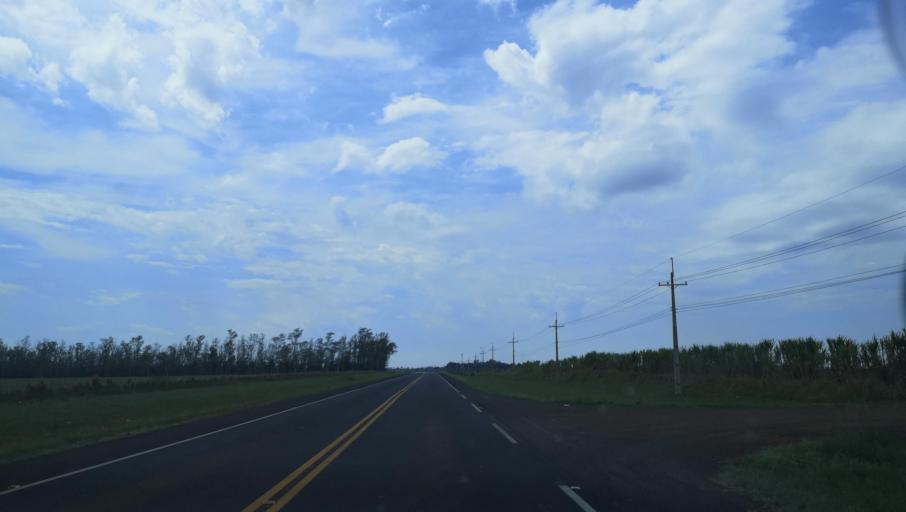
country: PY
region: Misiones
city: San Patricio
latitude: -26.9994
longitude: -56.7561
